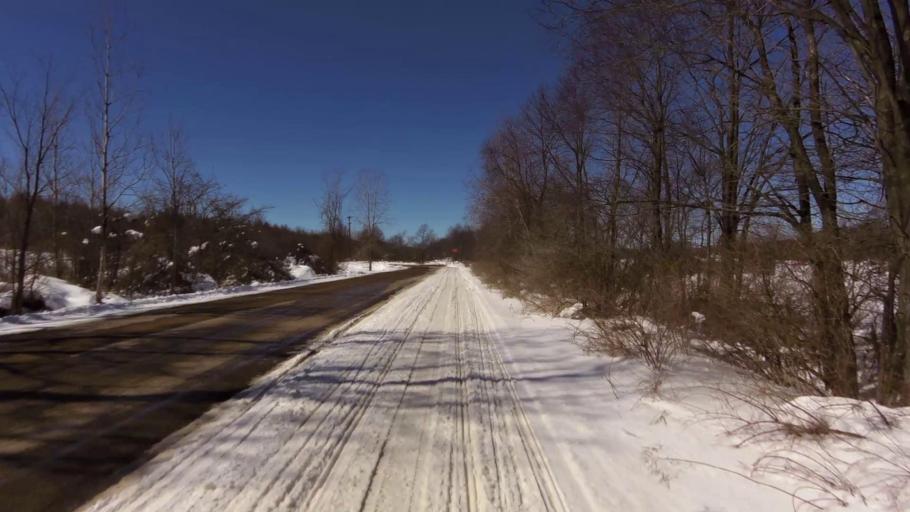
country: US
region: New York
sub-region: Cattaraugus County
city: Delevan
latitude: 42.4354
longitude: -78.4083
